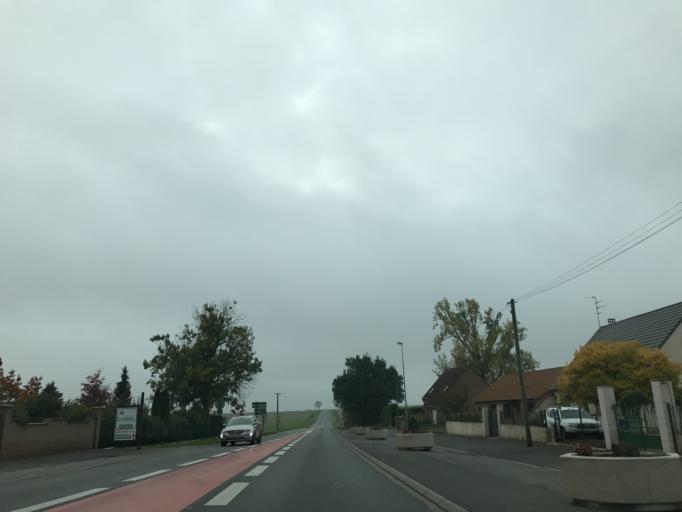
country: FR
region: Nord-Pas-de-Calais
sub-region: Departement du Pas-de-Calais
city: Beaurains
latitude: 50.2357
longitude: 2.8010
